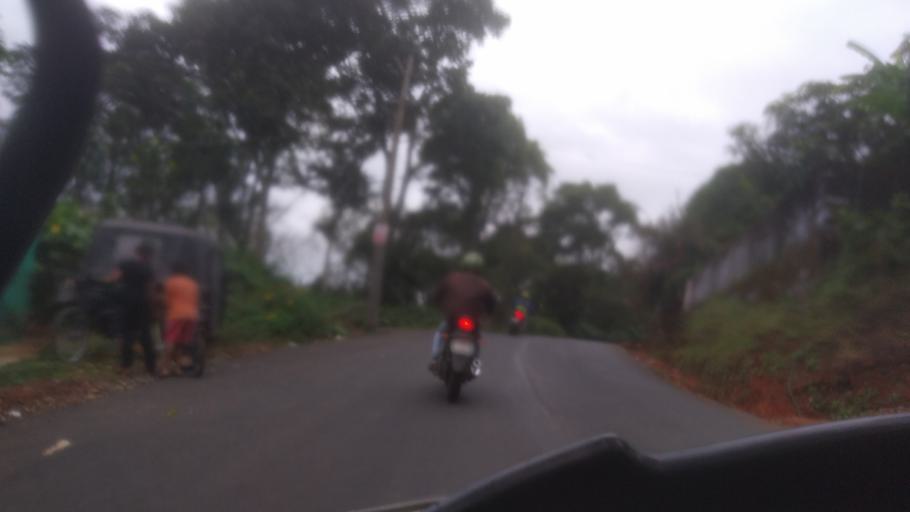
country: IN
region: Tamil Nadu
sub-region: Theni
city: Kombai
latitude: 9.8936
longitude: 77.1427
